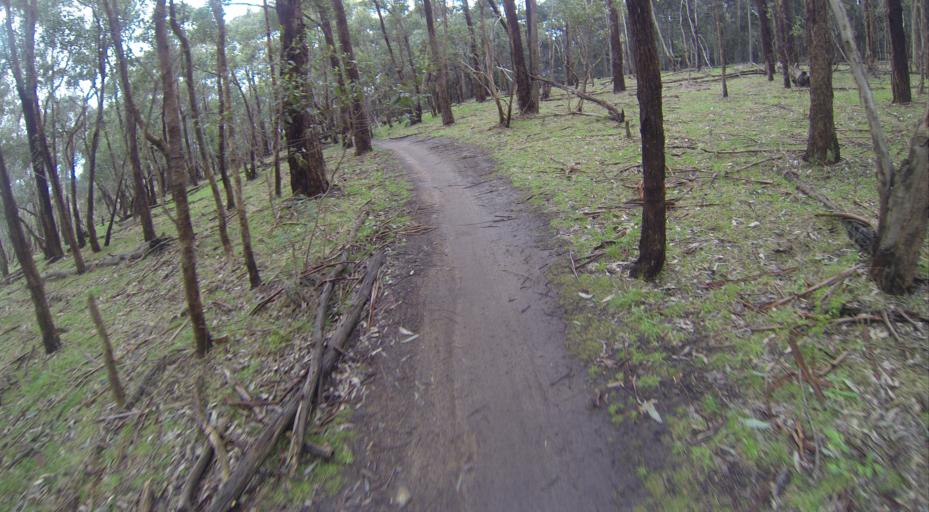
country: AU
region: Victoria
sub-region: Yarra Ranges
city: Lysterfield
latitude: -37.9610
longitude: 145.2907
